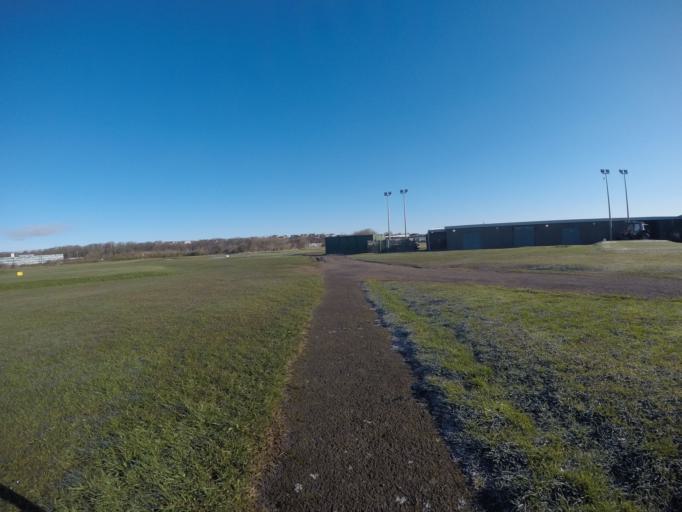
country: GB
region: Scotland
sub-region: North Ayrshire
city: Stevenston
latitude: 55.6355
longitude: -4.7629
